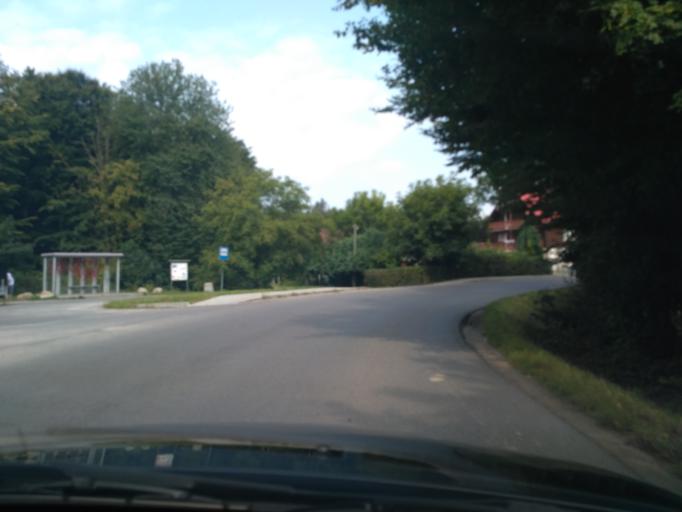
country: PL
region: Subcarpathian Voivodeship
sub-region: Powiat strzyzowski
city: Czudec
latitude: 49.9711
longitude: 21.8363
